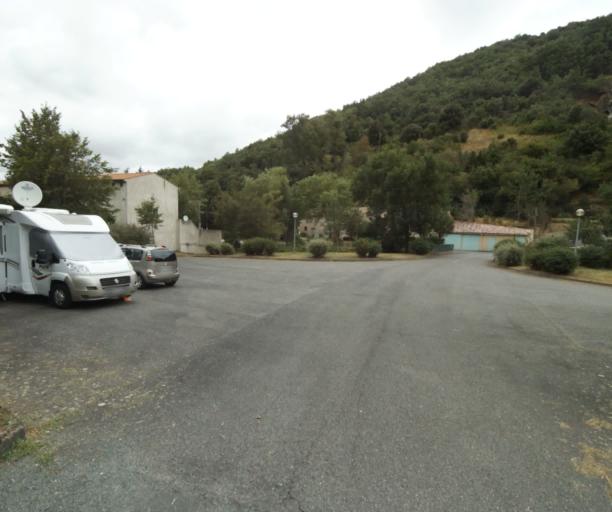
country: FR
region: Midi-Pyrenees
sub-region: Departement du Tarn
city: Soreze
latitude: 43.4396
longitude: 2.0643
